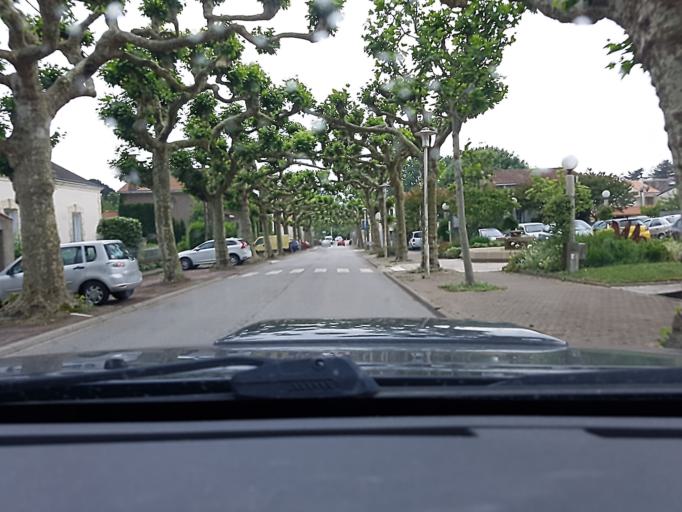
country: FR
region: Pays de la Loire
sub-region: Departement de la Vendee
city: Aizenay
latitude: 46.7389
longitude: -1.6080
